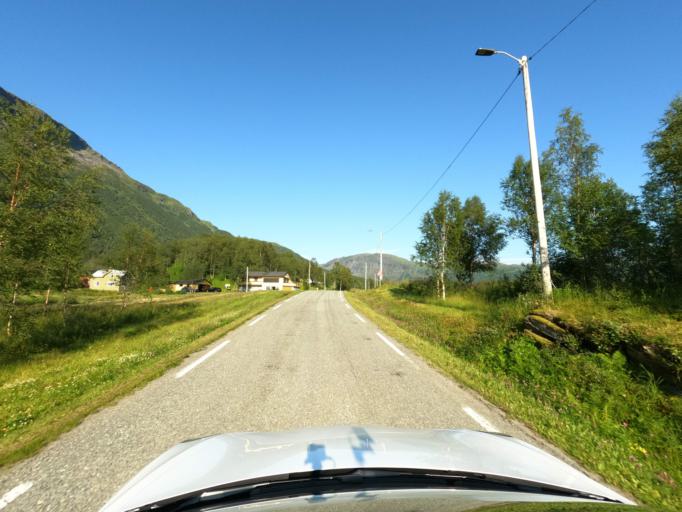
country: NO
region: Troms
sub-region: Gratangen
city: Gratangen
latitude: 68.5612
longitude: 17.6933
